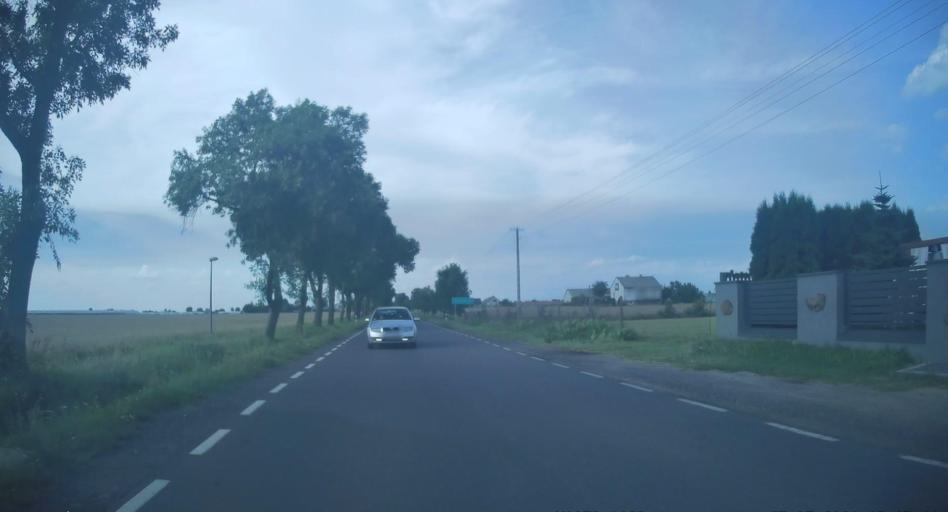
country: PL
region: Lodz Voivodeship
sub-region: Powiat tomaszowski
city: Rzeczyca
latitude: 51.6017
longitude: 20.2938
